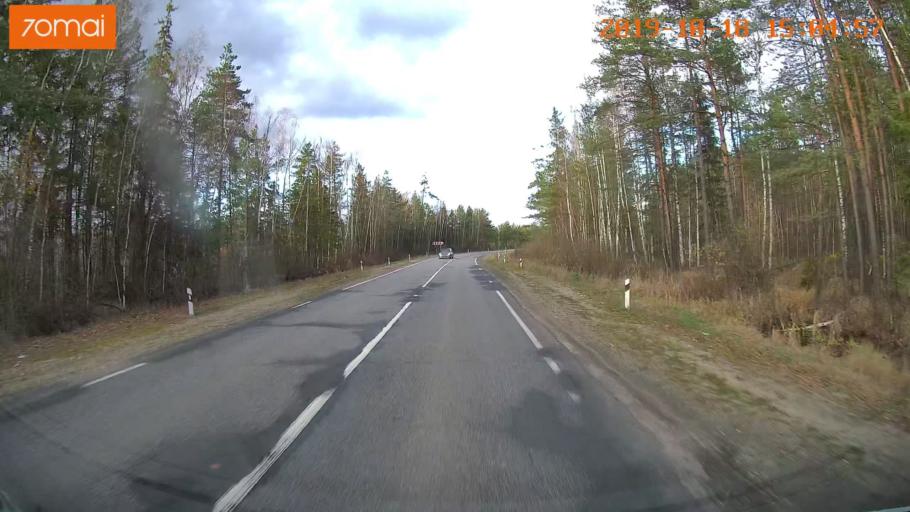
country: RU
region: Vladimir
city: Kurlovo
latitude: 55.5081
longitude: 40.5701
